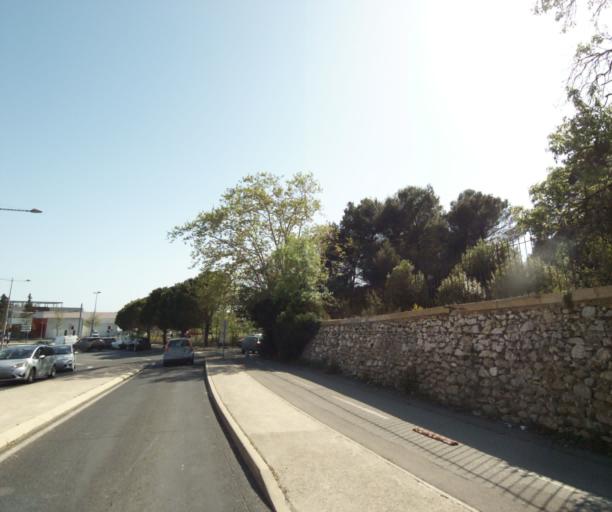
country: FR
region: Languedoc-Roussillon
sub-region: Departement de l'Herault
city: Grabels
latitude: 43.6401
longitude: 3.8280
